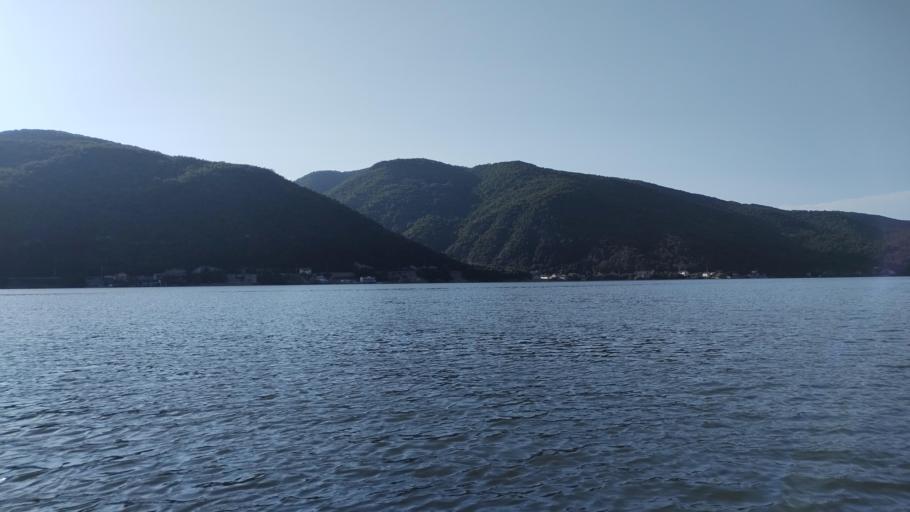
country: RO
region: Mehedinti
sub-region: Comuna Dubova
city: Dubova
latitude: 44.5634
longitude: 22.2354
